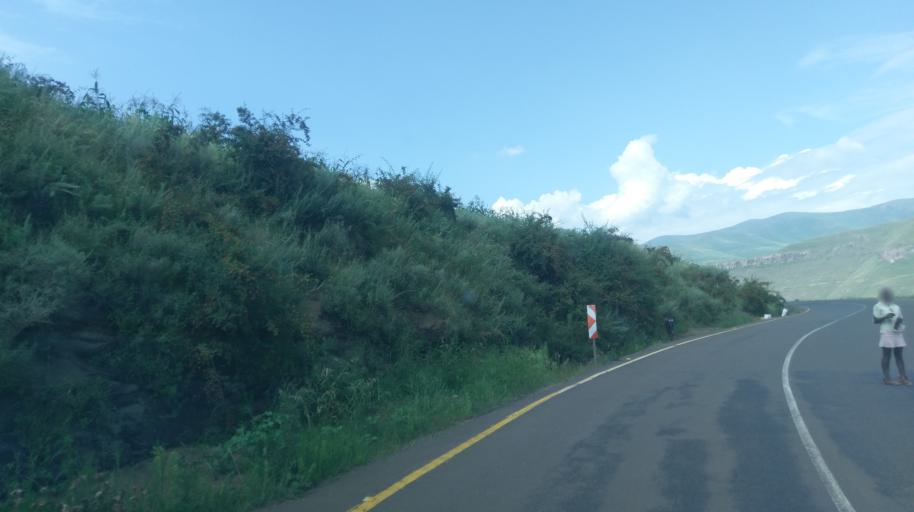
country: LS
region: Thaba-Tseka
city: Thaba-Tseka
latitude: -29.1482
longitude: 28.4889
